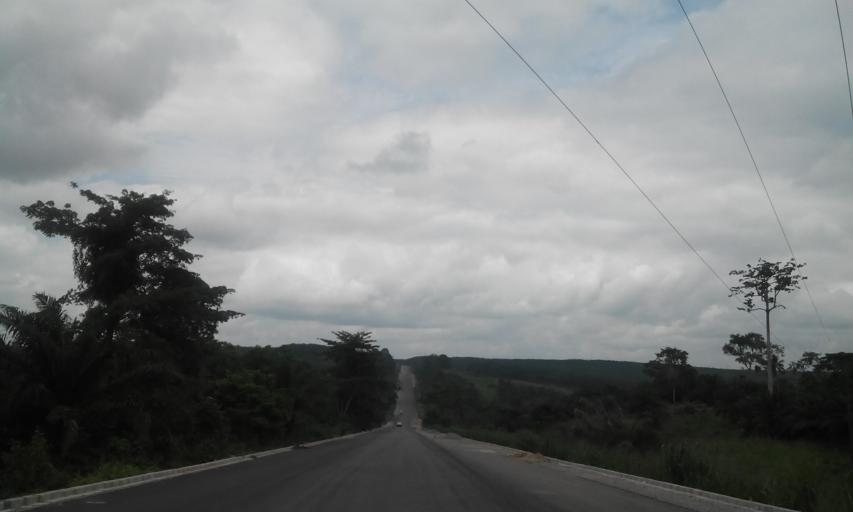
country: CI
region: Sud-Comoe
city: Mafere
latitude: 5.3121
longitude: -3.0489
